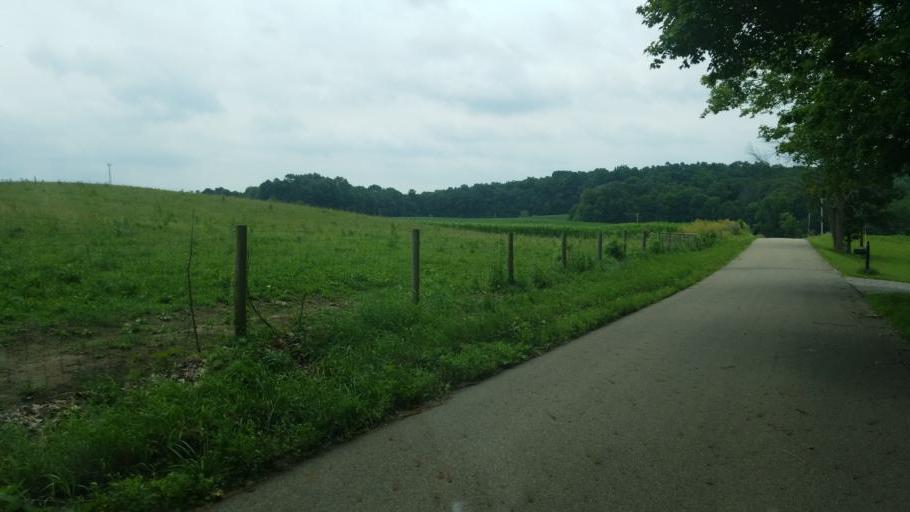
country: US
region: Ohio
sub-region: Licking County
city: Utica
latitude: 40.1836
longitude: -82.4614
